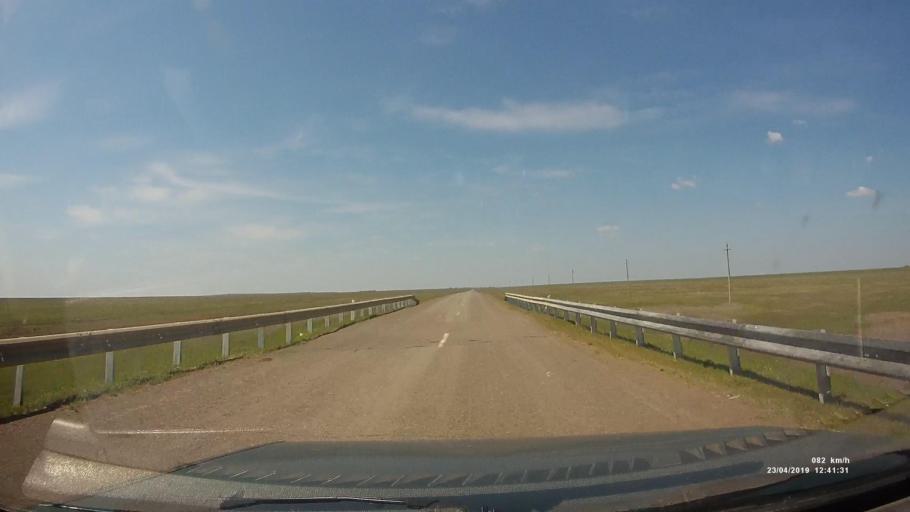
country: RU
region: Kalmykiya
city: Yashalta
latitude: 46.4491
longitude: 42.6790
